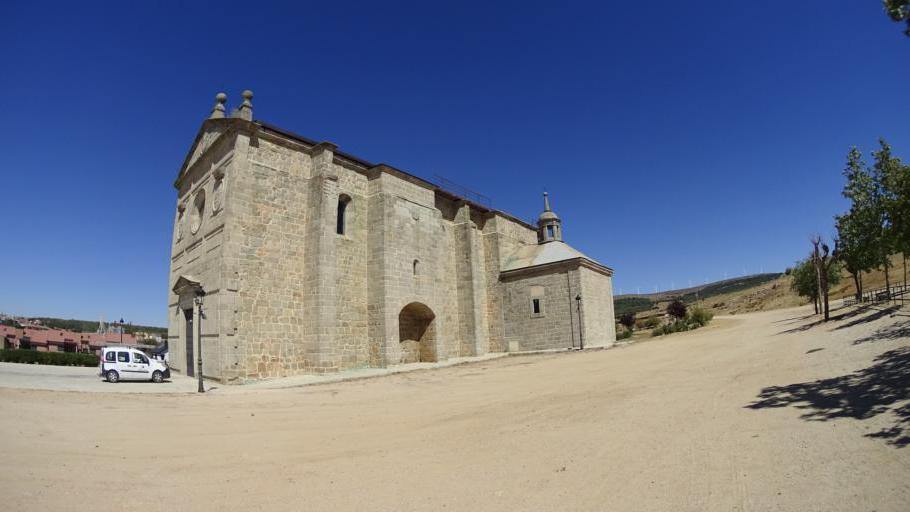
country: ES
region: Castille and Leon
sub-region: Provincia de Avila
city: Las Navas del Marques
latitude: 40.6054
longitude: -4.3262
